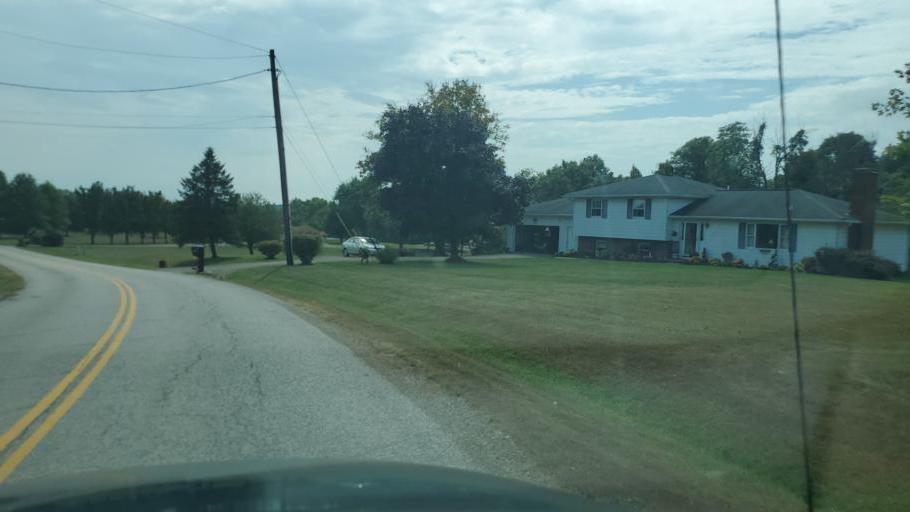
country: US
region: Ohio
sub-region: Muskingum County
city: Zanesville
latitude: 39.9524
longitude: -82.1448
